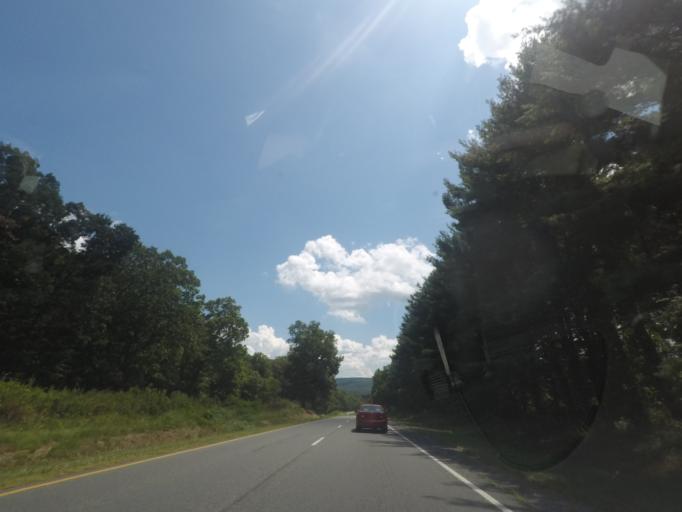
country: US
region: Virginia
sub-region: Warren County
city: Shenandoah Farms
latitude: 39.0481
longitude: -78.0120
